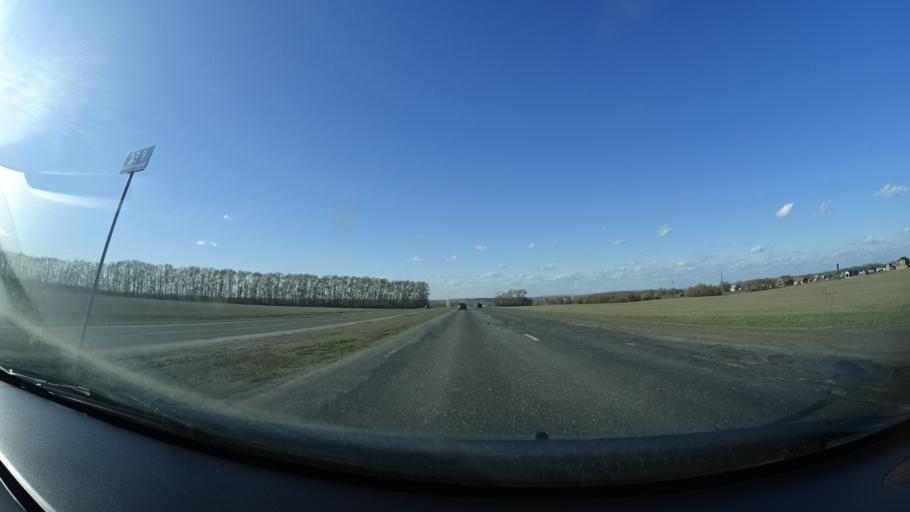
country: RU
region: Bashkortostan
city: Kabakovo
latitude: 54.4697
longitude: 55.9130
